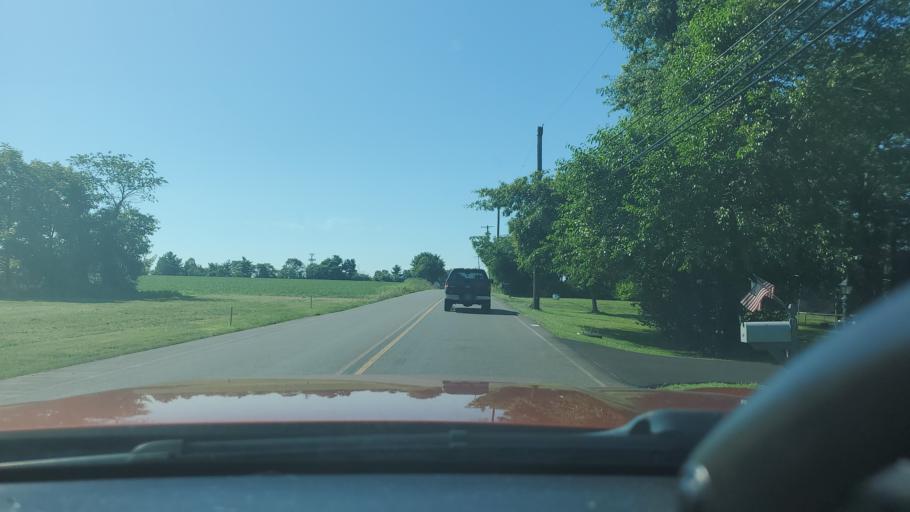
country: US
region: Pennsylvania
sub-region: Montgomery County
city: Limerick
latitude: 40.2386
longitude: -75.5275
